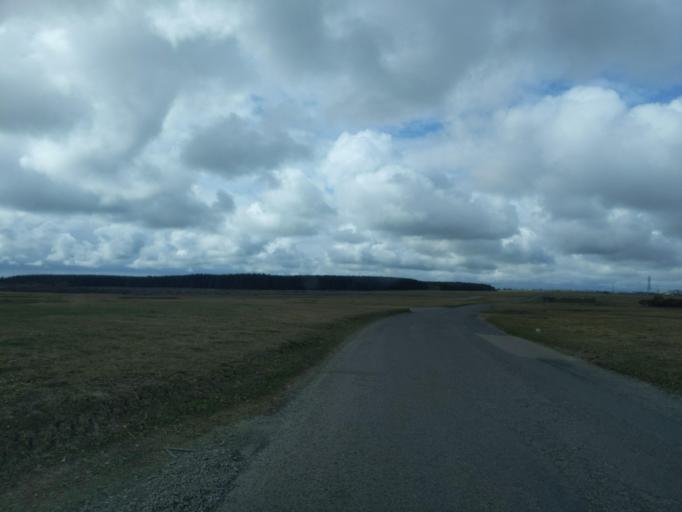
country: GB
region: England
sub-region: Cornwall
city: Camelford
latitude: 50.6302
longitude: -4.6050
